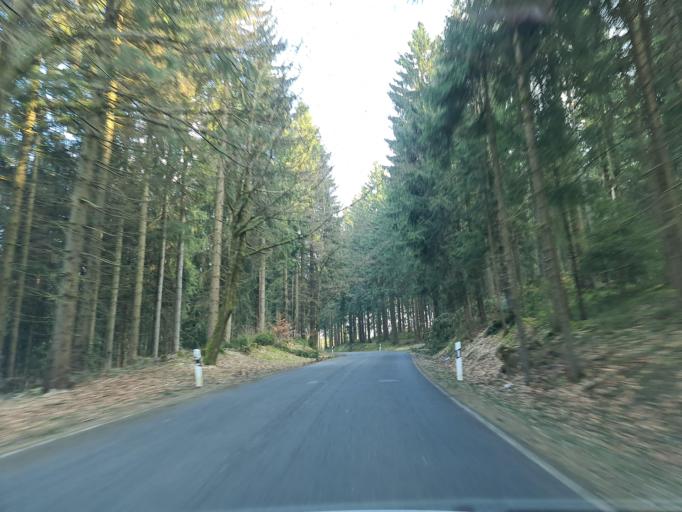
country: DE
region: Saxony
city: Muldenhammer
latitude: 50.4941
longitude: 12.4551
